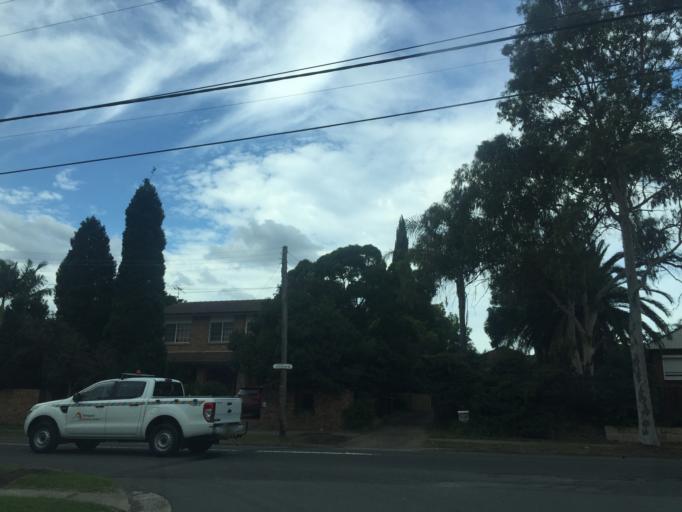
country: AU
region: New South Wales
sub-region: Blacktown
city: Blacktown
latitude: -33.7867
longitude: 150.8994
